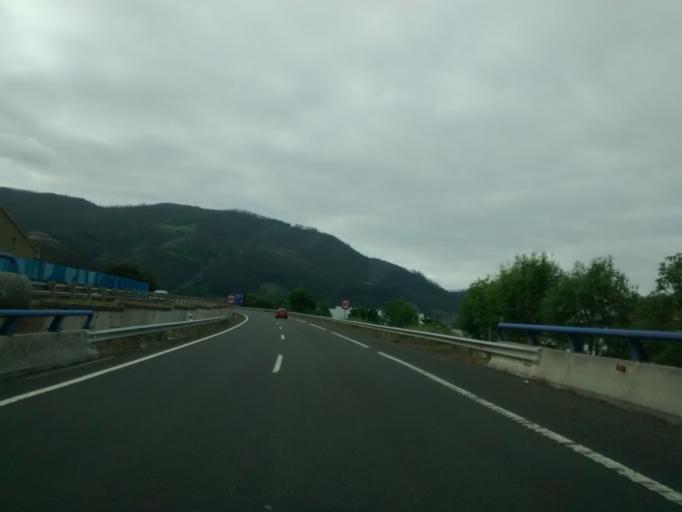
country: ES
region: Cantabria
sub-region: Provincia de Cantabria
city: Los Corrales de Buelna
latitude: 43.2725
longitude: -4.0750
